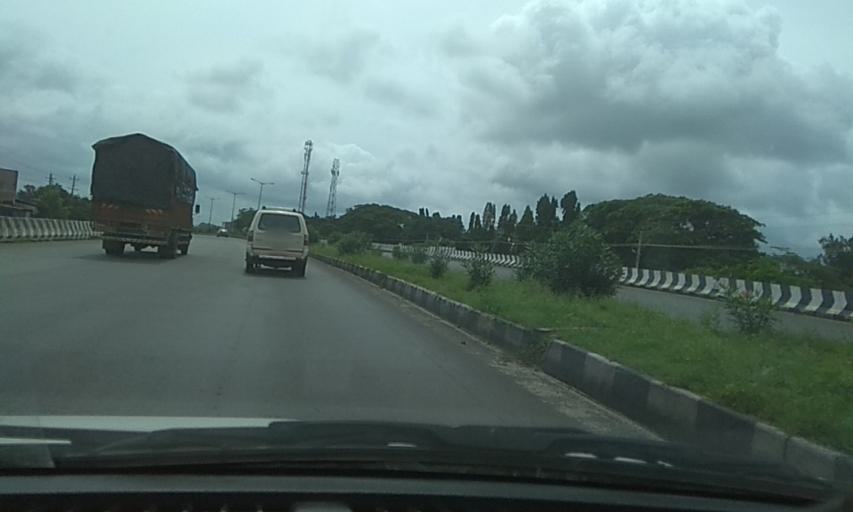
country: IN
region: Karnataka
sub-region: Davanagere
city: Mayakonda
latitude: 14.3781
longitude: 76.0958
